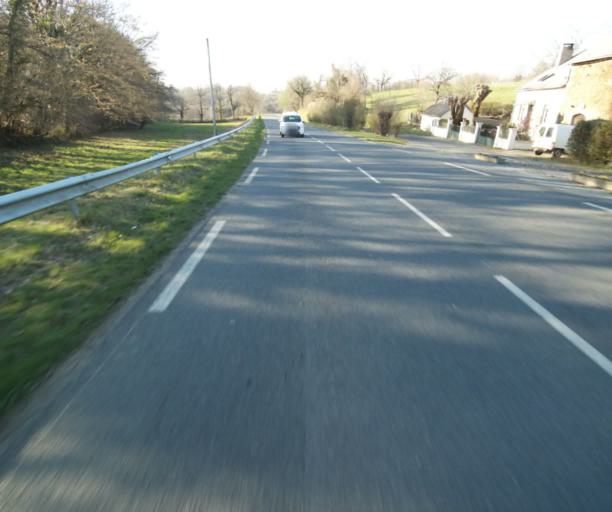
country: FR
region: Limousin
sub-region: Departement de la Correze
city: Seilhac
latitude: 45.3896
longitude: 1.7213
